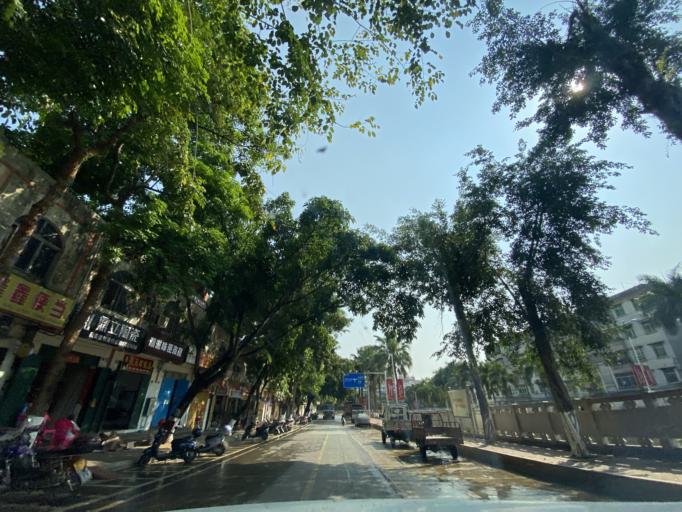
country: CN
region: Hainan
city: Chongshan
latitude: 18.7833
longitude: 109.5139
